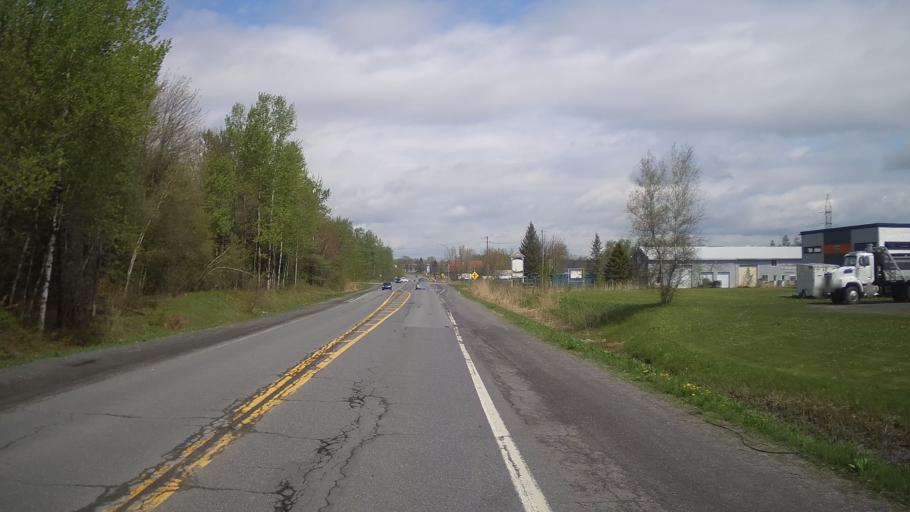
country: CA
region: Quebec
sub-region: Monteregie
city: Cowansville
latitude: 45.2020
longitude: -72.7650
